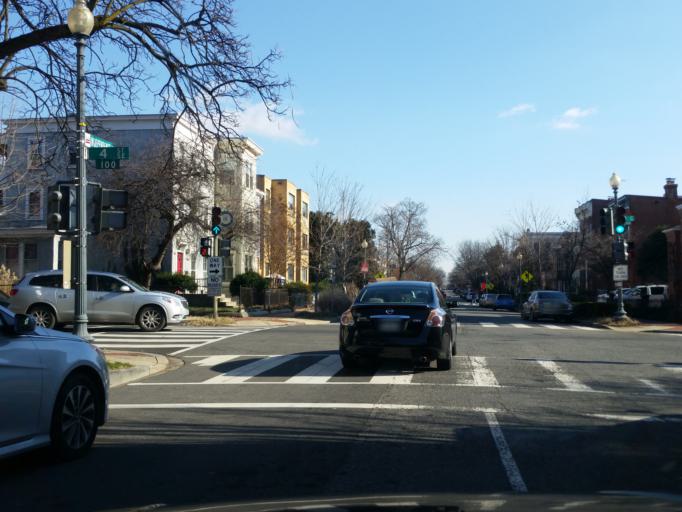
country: US
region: Washington, D.C.
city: Washington, D.C.
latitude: 38.8876
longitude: -77.0008
